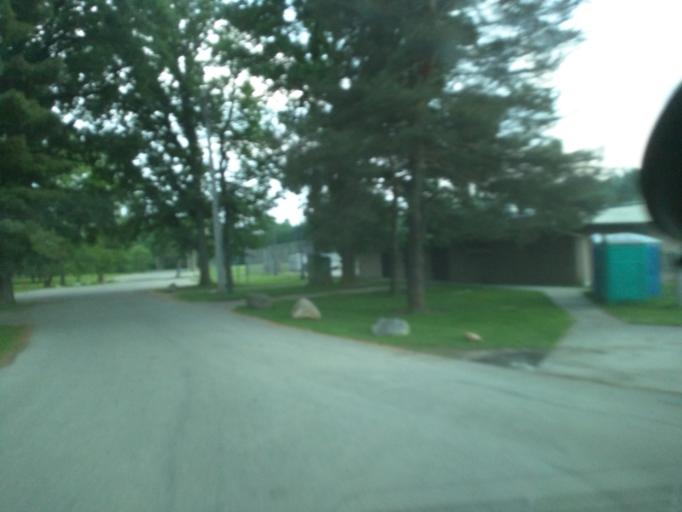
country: US
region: Michigan
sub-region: Ingham County
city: Lansing
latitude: 42.7049
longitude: -84.5605
